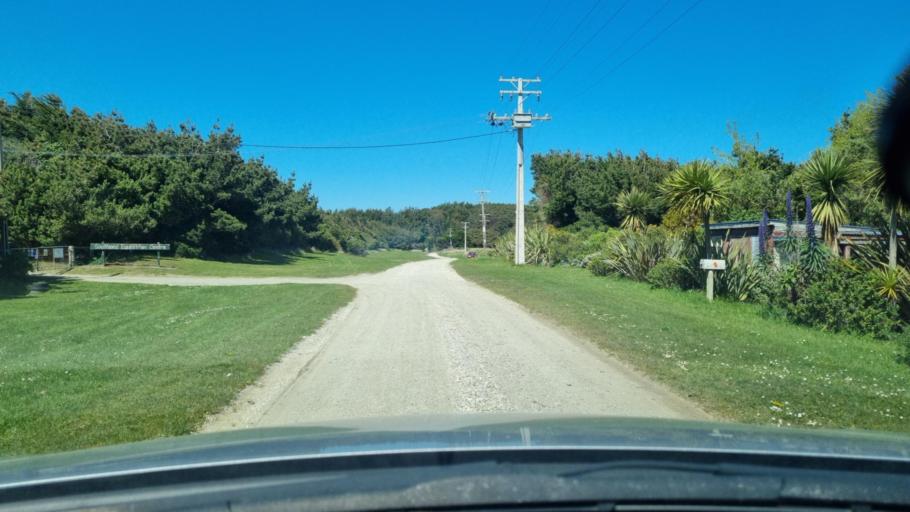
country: NZ
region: Southland
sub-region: Invercargill City
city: Invercargill
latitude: -46.4386
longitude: 168.2390
